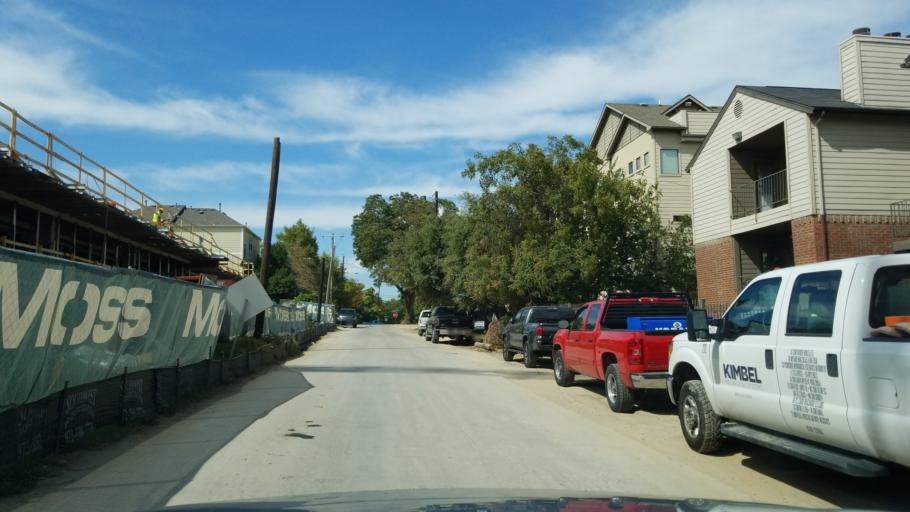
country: US
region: Texas
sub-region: Dallas County
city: Highland Park
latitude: 32.8076
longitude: -96.7306
